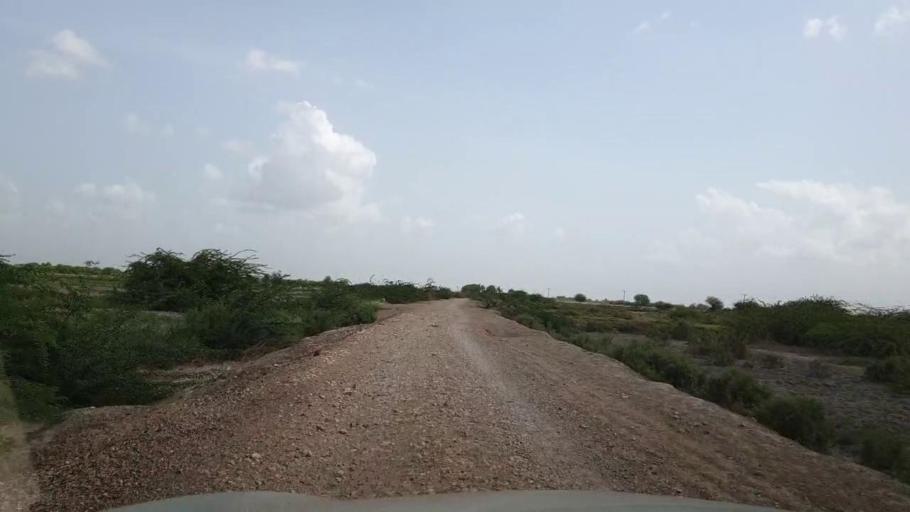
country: PK
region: Sindh
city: Kadhan
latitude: 24.3983
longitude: 68.7971
